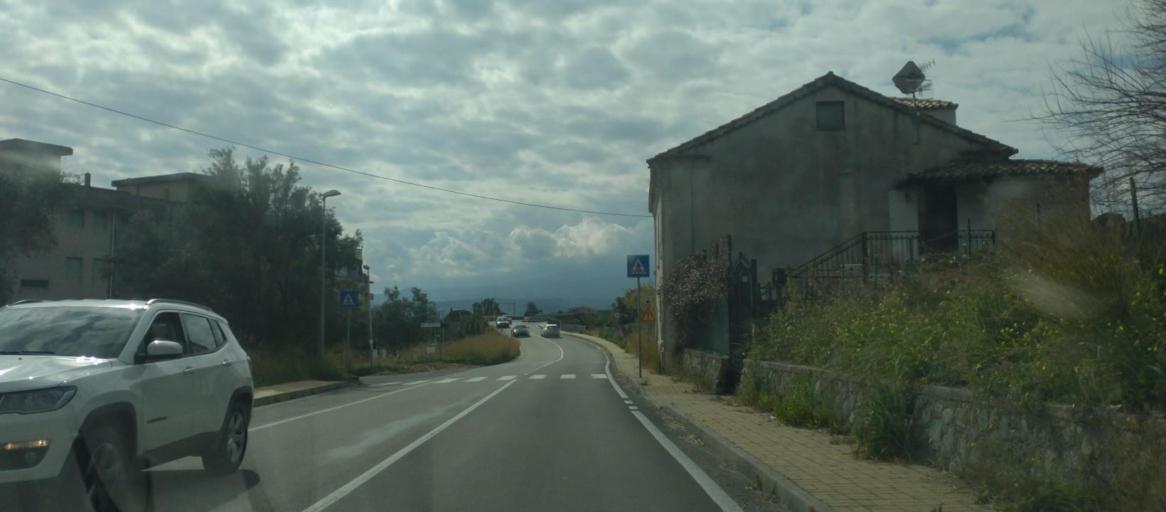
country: IT
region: Calabria
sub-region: Provincia di Catanzaro
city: Montepaone Lido
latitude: 38.7413
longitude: 16.5490
